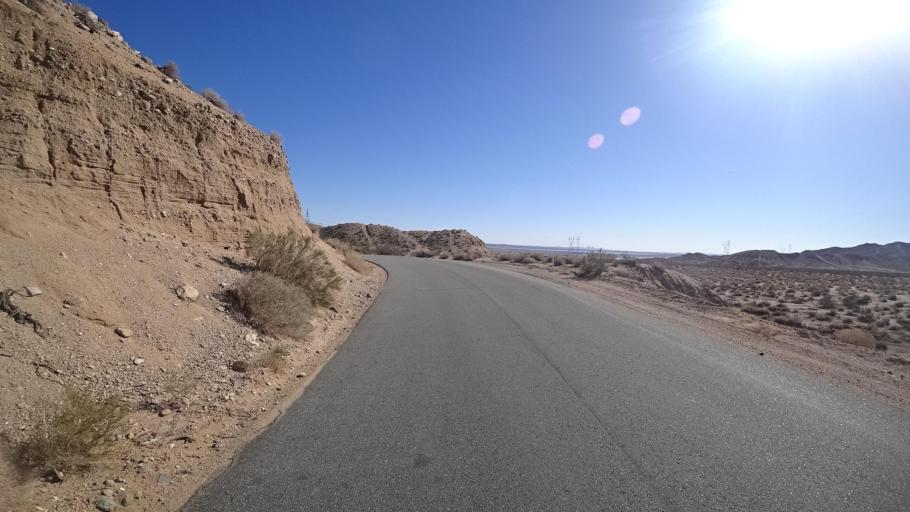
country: US
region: California
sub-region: Kern County
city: California City
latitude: 35.3075
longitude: -118.0130
